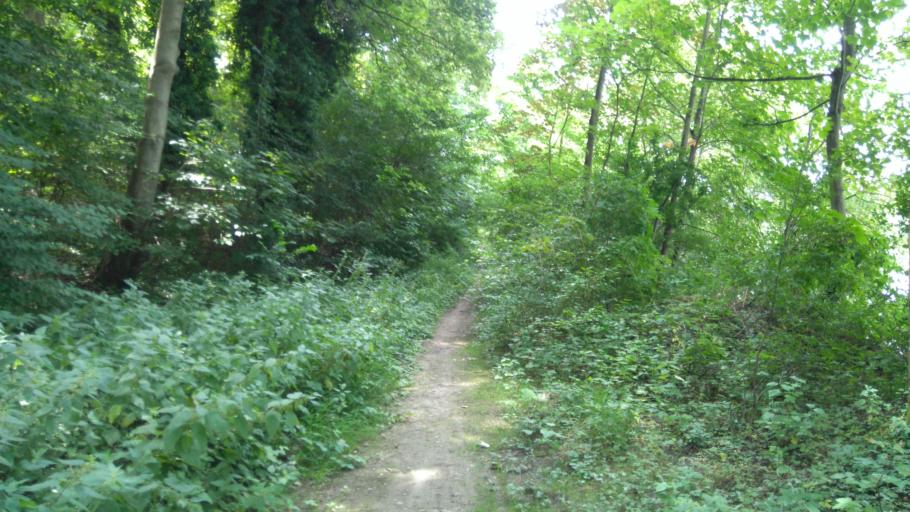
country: FR
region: Picardie
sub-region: Departement de l'Oise
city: Thiverny
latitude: 49.2421
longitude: 2.4530
